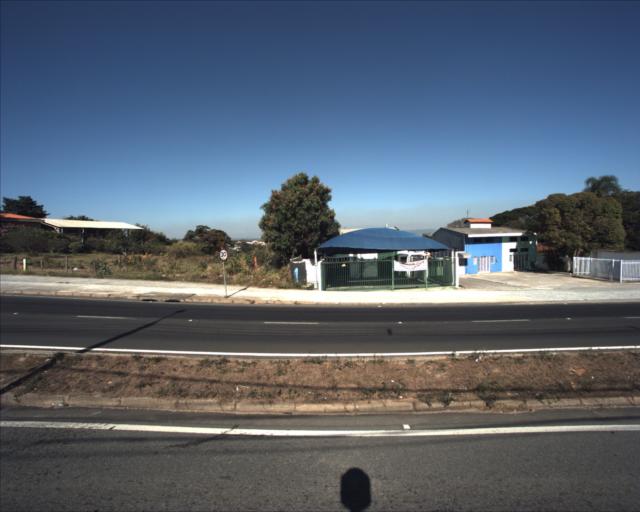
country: BR
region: Sao Paulo
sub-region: Sorocaba
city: Sorocaba
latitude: -23.4001
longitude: -47.3800
